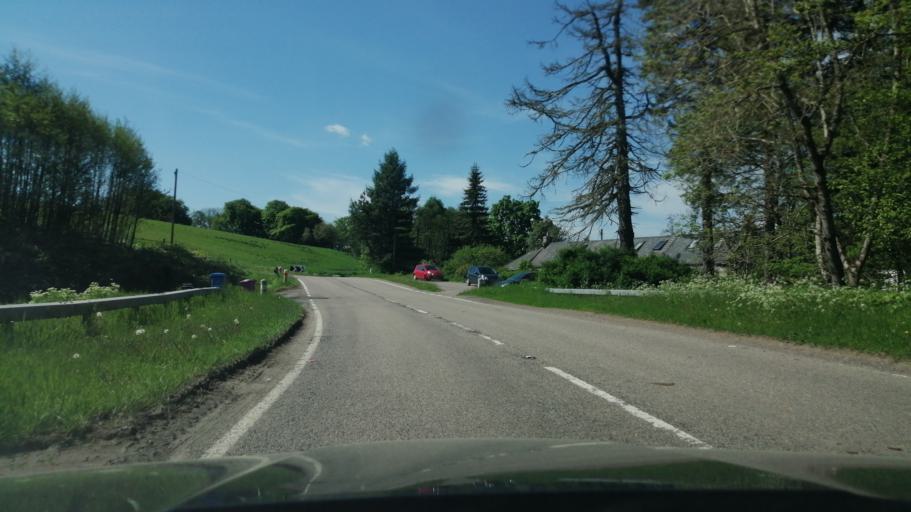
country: GB
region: Scotland
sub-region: Moray
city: Dufftown
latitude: 57.5044
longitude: -3.1292
